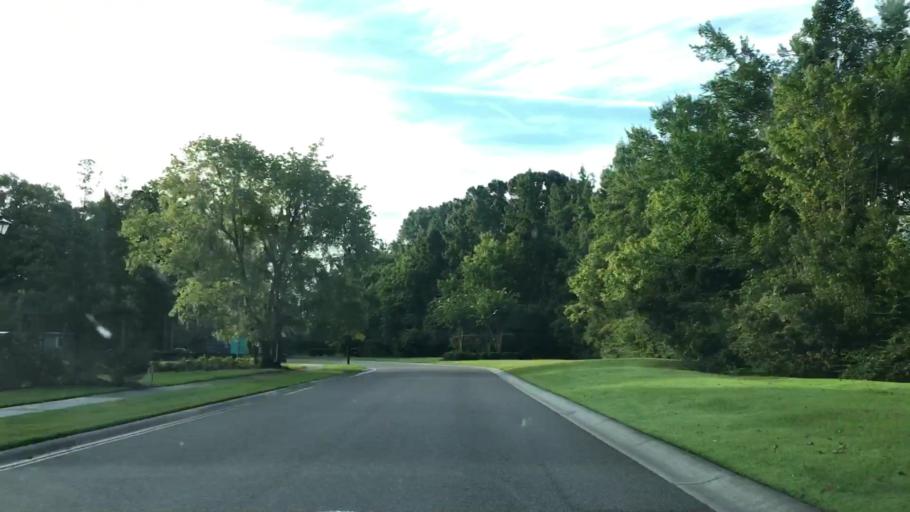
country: US
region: South Carolina
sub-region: Charleston County
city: Shell Point
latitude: 32.8366
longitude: -80.0715
